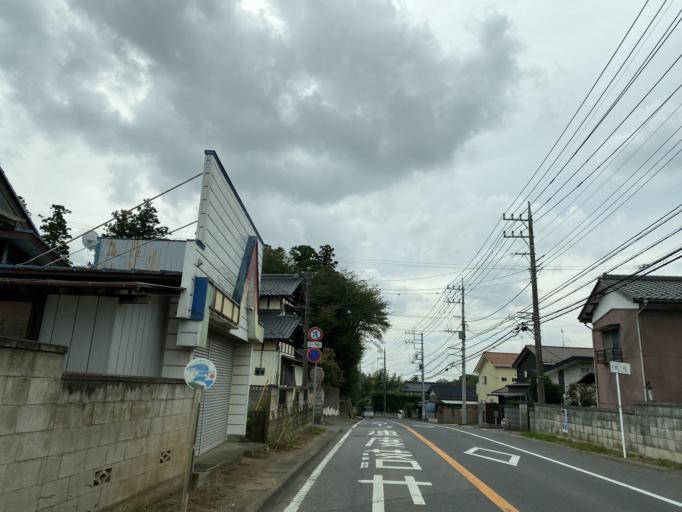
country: JP
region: Ibaraki
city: Mitsukaido
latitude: 35.9881
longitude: 140.0436
